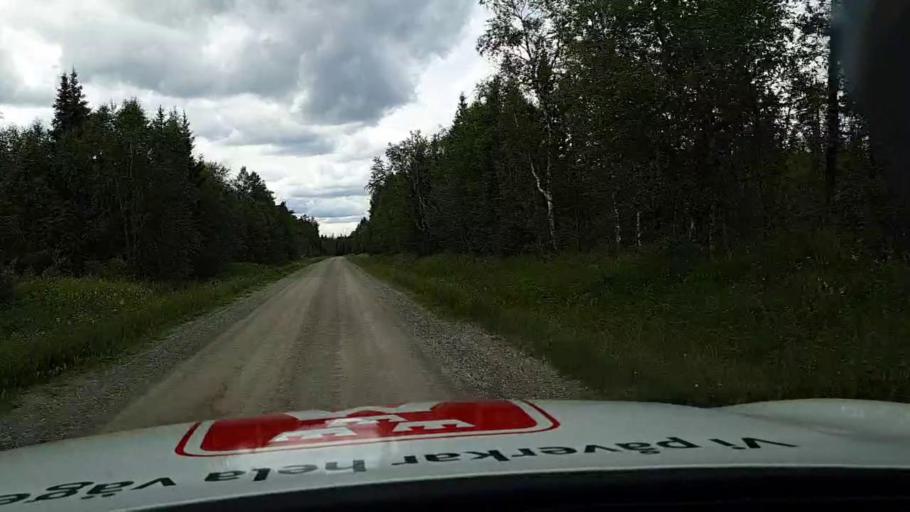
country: SE
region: Jaemtland
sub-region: Stroemsunds Kommun
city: Stroemsund
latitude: 63.3132
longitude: 15.5166
